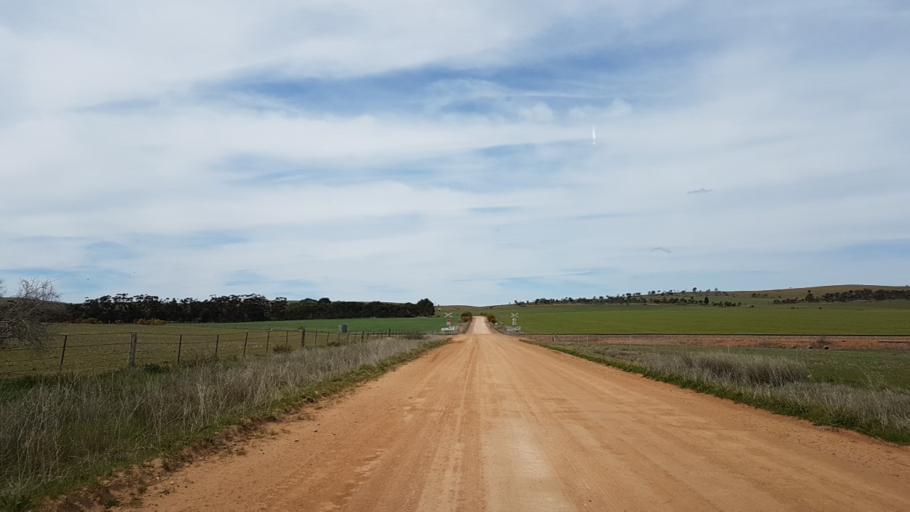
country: AU
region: South Australia
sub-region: Northern Areas
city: Jamestown
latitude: -33.1076
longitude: 138.6221
